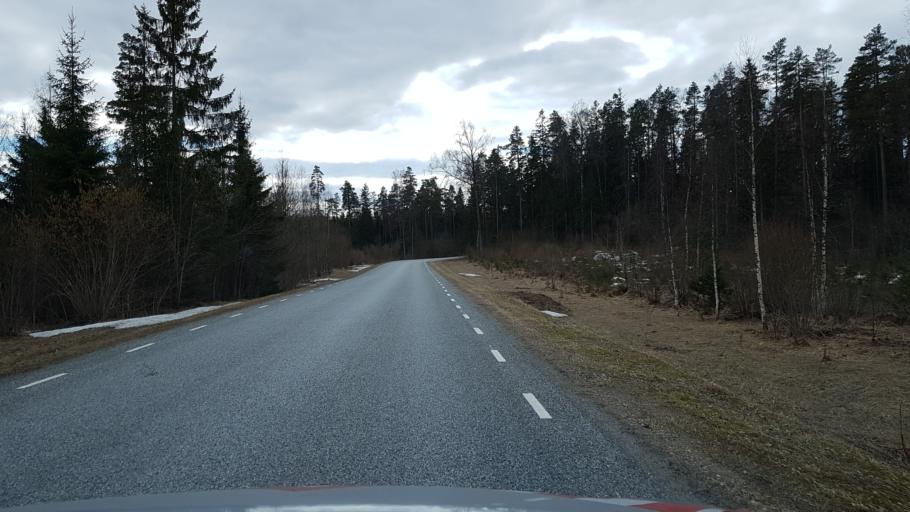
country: EE
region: Laeaene-Virumaa
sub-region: Tamsalu vald
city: Tamsalu
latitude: 59.2331
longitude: 26.1710
